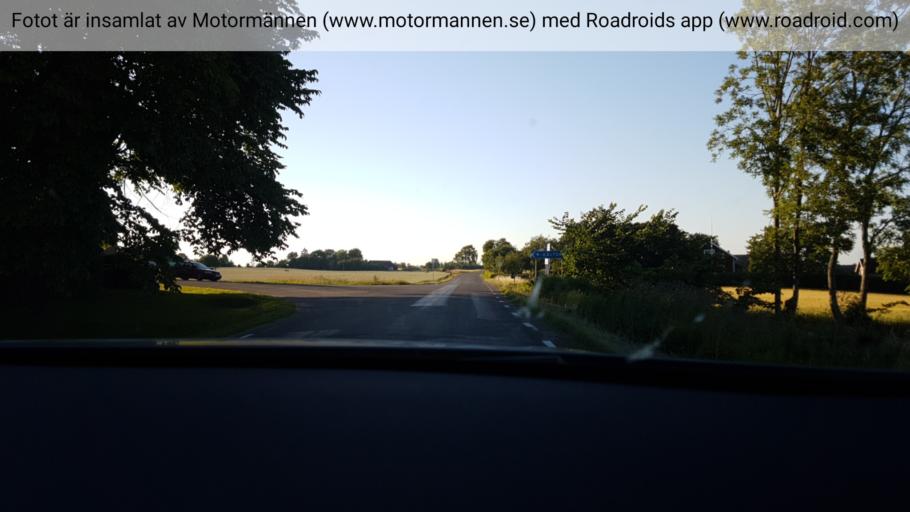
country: SE
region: Vaestra Goetaland
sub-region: Skovde Kommun
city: Skultorp
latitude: 58.2383
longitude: 13.7899
